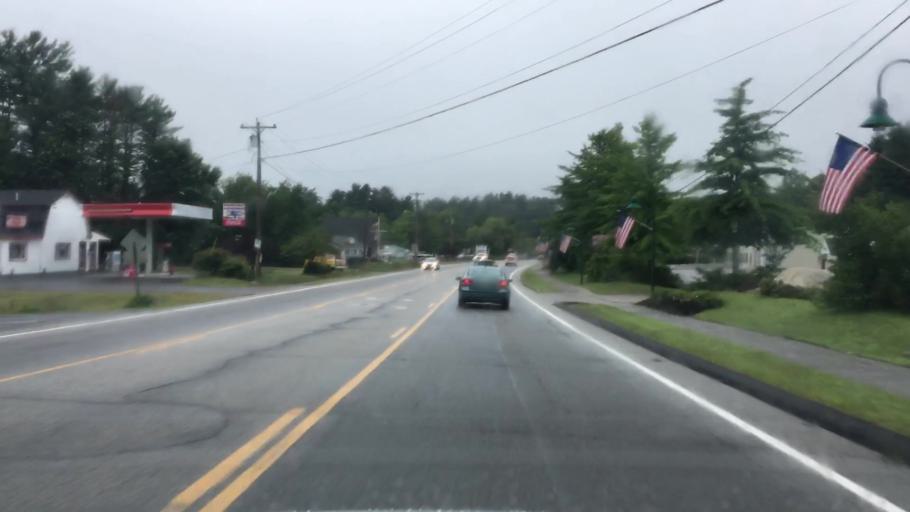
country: US
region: Maine
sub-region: Cumberland County
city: Raymond
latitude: 43.8867
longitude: -70.4647
